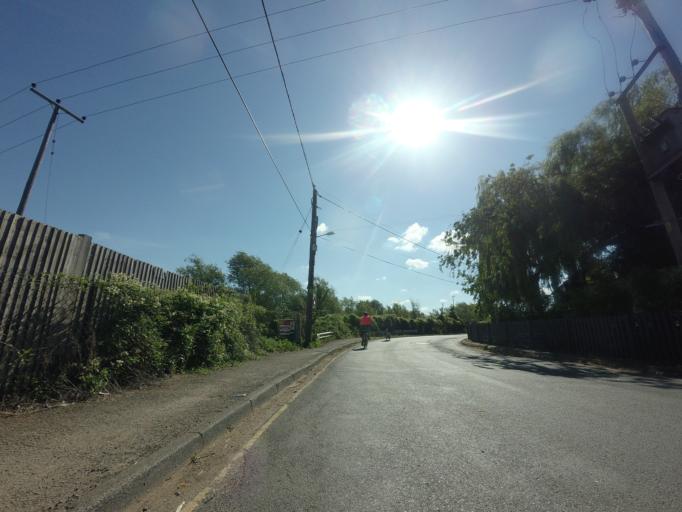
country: GB
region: England
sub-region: Kent
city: Strood
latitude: 51.4294
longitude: 0.4624
